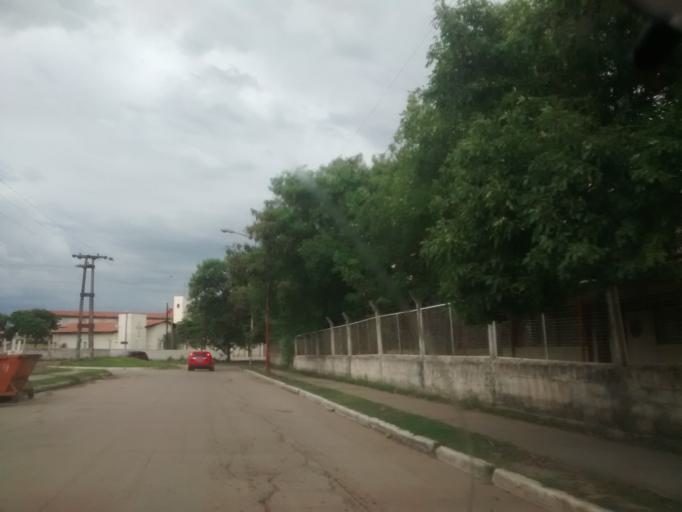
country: AR
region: Chaco
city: Fontana
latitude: -27.4426
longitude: -59.0166
